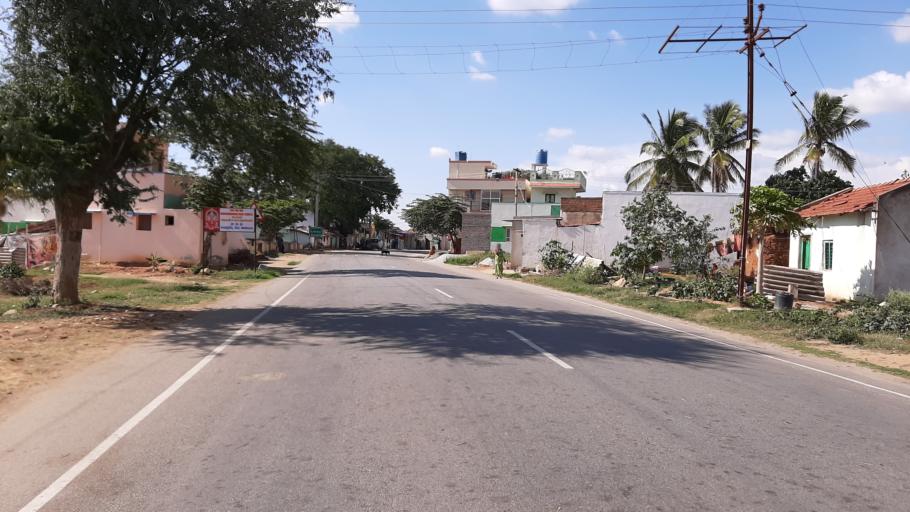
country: IN
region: Tamil Nadu
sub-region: Krishnagiri
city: Denkanikota
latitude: 12.5570
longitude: 77.7849
